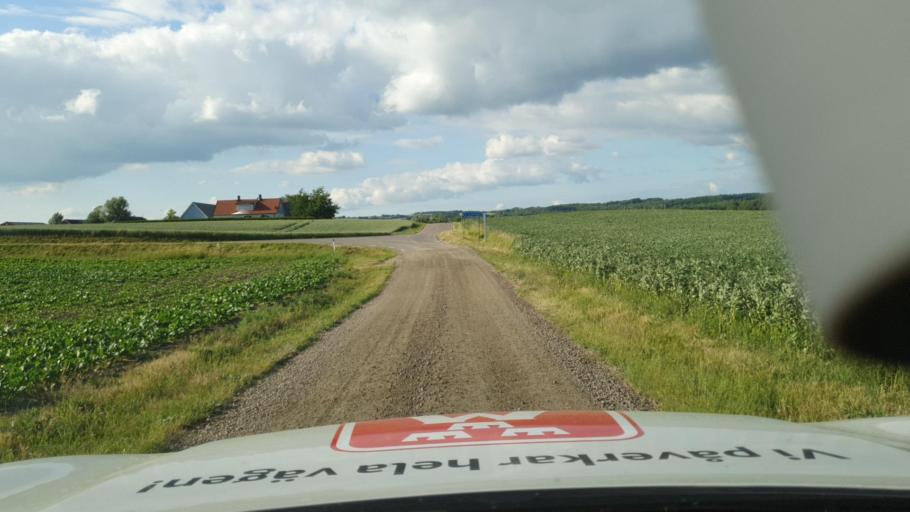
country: SE
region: Skane
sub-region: Skurups Kommun
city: Rydsgard
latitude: 55.5025
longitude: 13.5775
